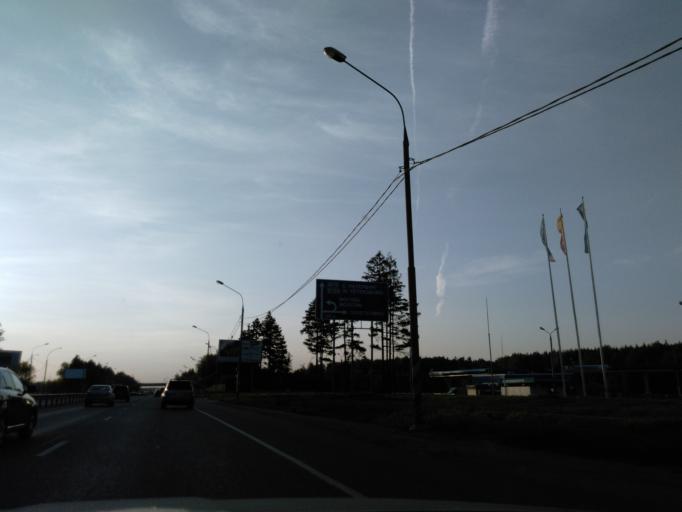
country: RU
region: Moskovskaya
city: Novopodrezkovo
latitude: 55.9630
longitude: 37.3320
